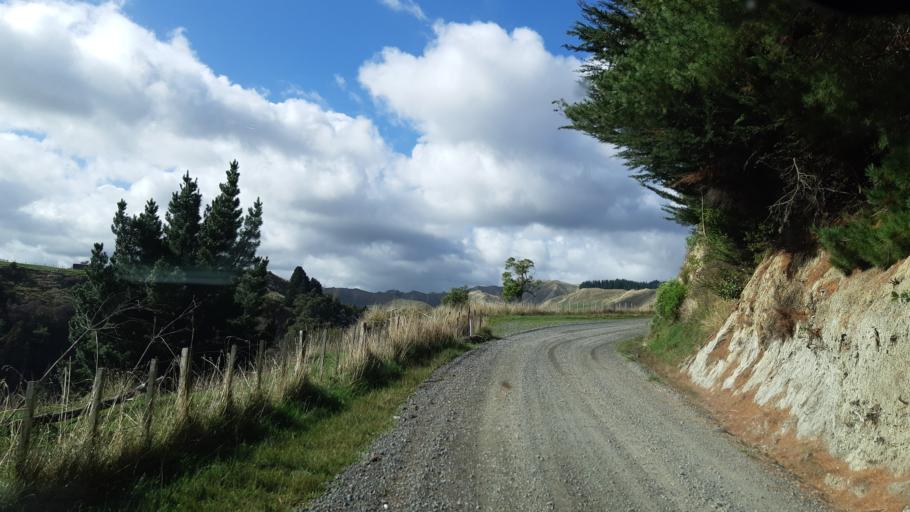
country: NZ
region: Manawatu-Wanganui
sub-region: Ruapehu District
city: Waiouru
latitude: -39.7585
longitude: 175.6669
